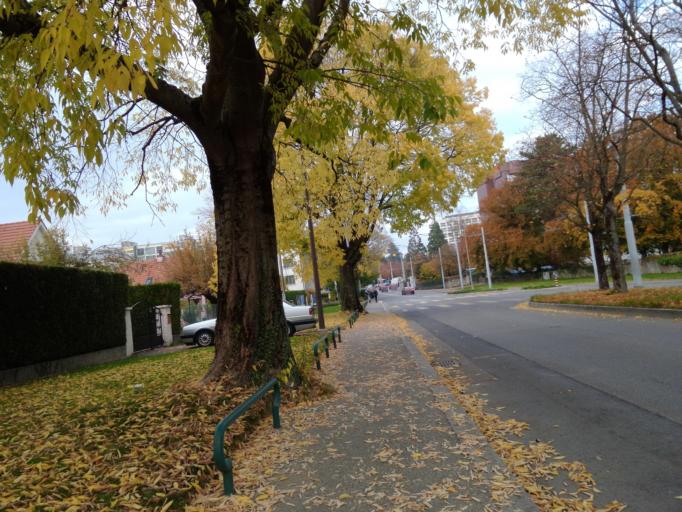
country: CH
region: Geneva
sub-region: Geneva
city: Les Avanchets
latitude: 46.2144
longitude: 6.1174
